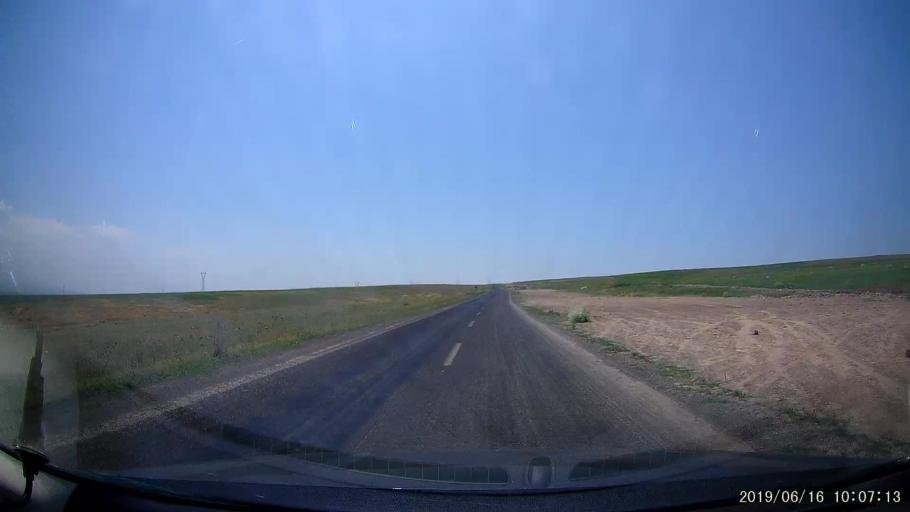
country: TR
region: Kars
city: Digor
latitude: 40.2467
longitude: 43.5529
